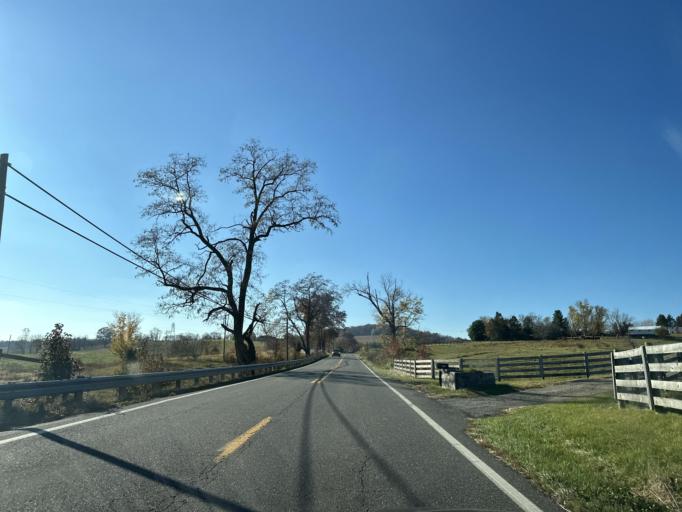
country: US
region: Virginia
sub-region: Rockingham County
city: Bridgewater
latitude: 38.3796
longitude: -78.9894
